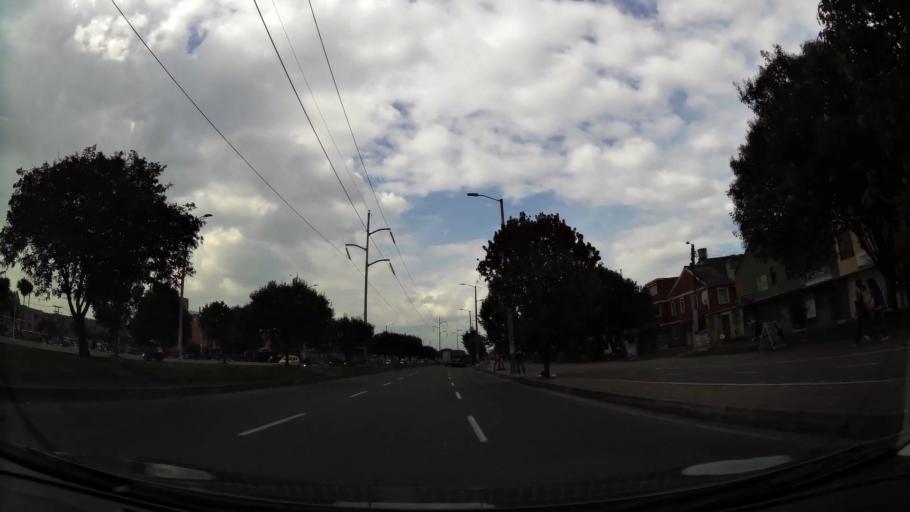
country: CO
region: Cundinamarca
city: Cota
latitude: 4.7395
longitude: -74.0992
